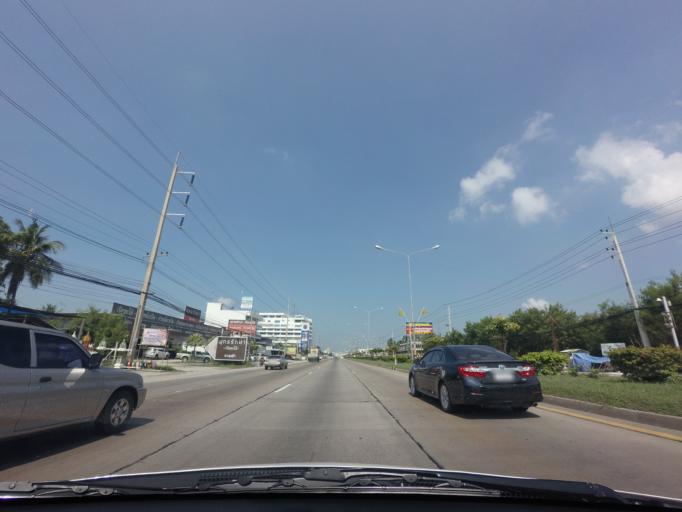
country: TH
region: Nakhon Pathom
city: Nakhon Chai Si
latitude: 13.7792
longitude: 100.1770
